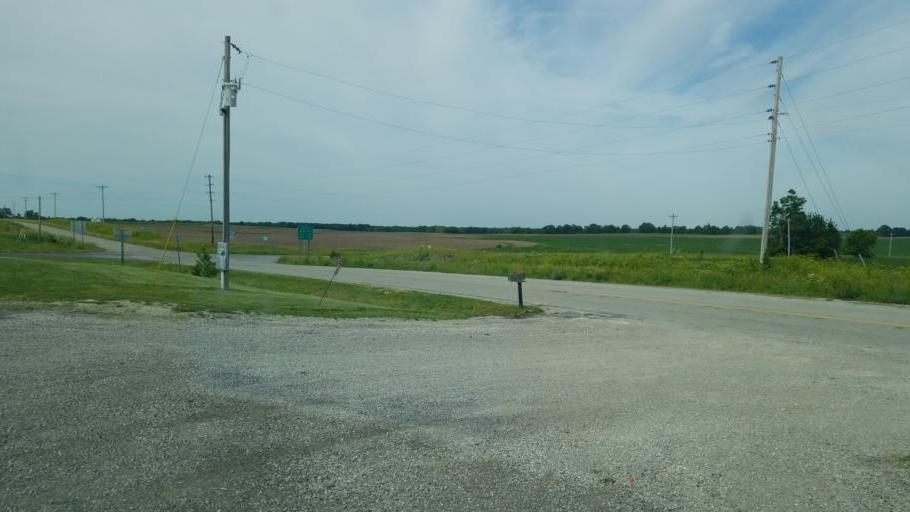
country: US
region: Missouri
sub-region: Saline County
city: Marshall
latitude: 38.9556
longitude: -93.0871
